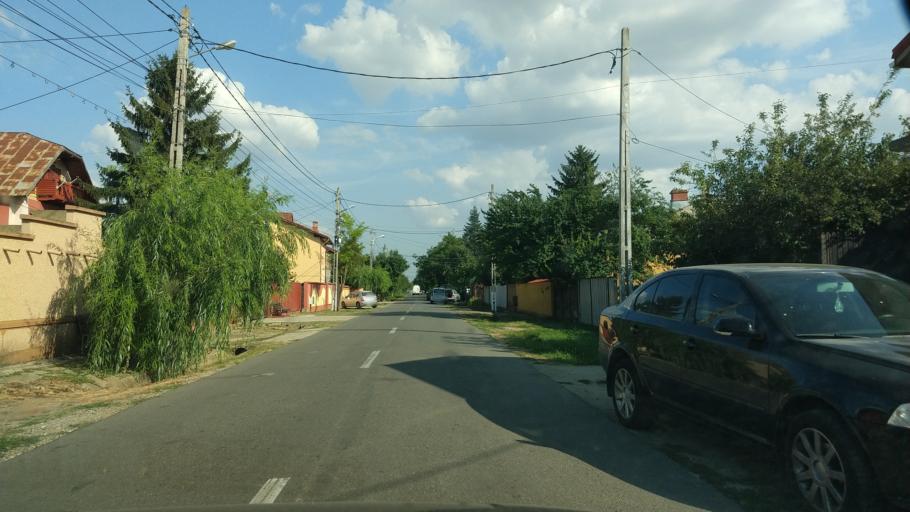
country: RO
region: Ilfov
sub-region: Comuna Afumati
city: Afumati
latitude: 44.5298
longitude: 26.2442
